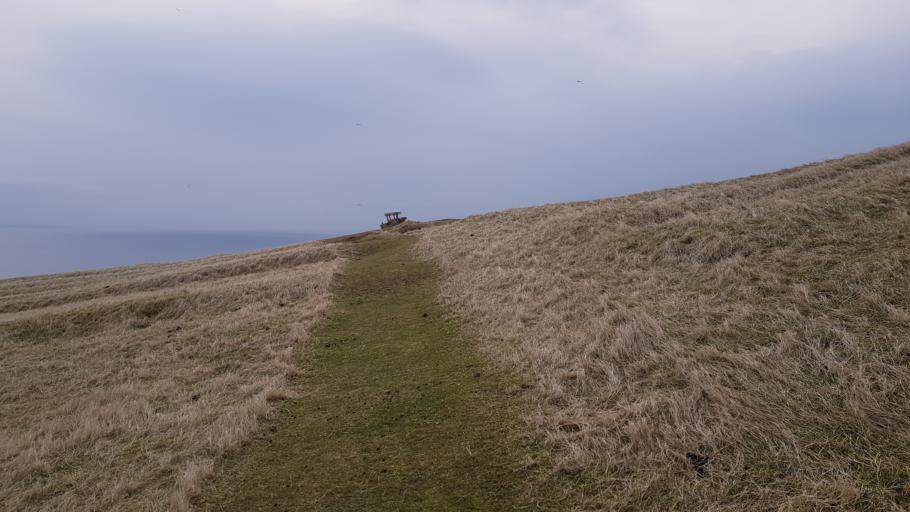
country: FO
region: Vagar
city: Sorvagur
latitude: 62.1109
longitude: -7.4429
